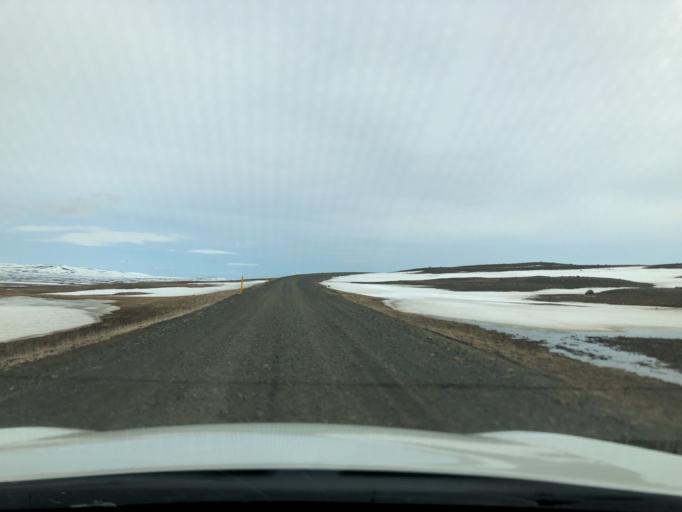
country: IS
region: East
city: Egilsstadir
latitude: 65.3078
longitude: -15.3860
